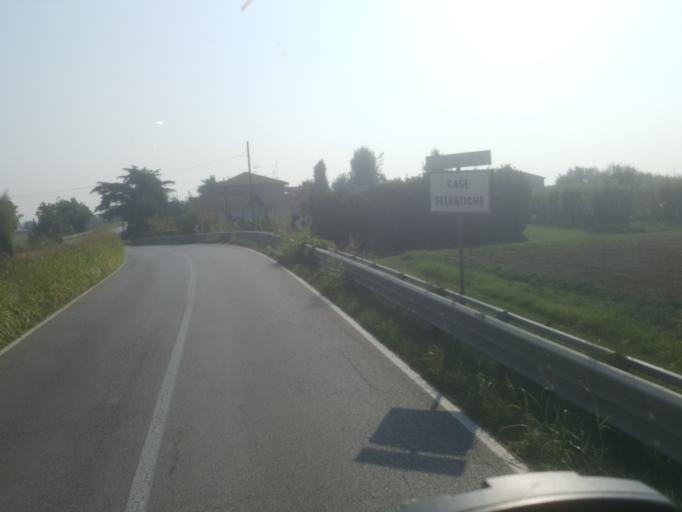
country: IT
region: Emilia-Romagna
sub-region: Provincia di Ferrara
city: San Biagio
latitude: 44.5826
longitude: 11.8968
